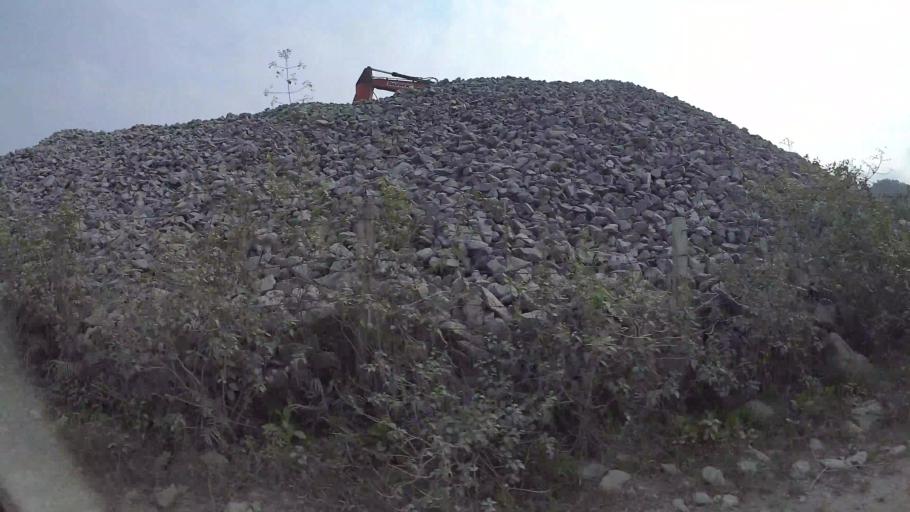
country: VN
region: Da Nang
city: Lien Chieu
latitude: 16.0442
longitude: 108.1471
